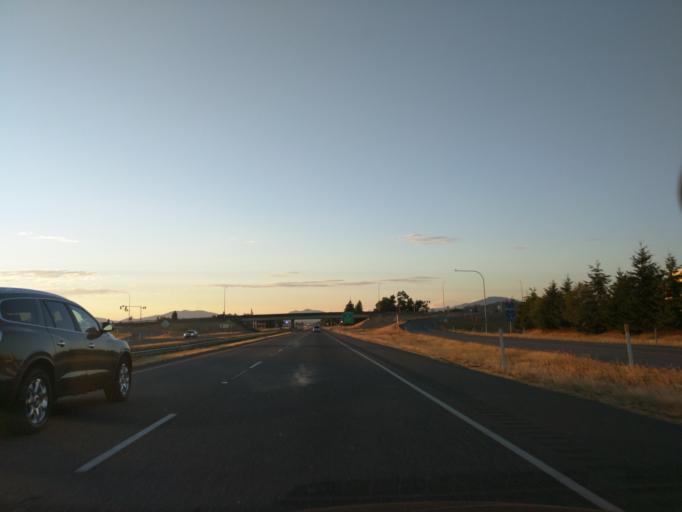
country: US
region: Washington
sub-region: Skagit County
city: Mount Vernon
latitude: 48.4497
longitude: -122.3411
